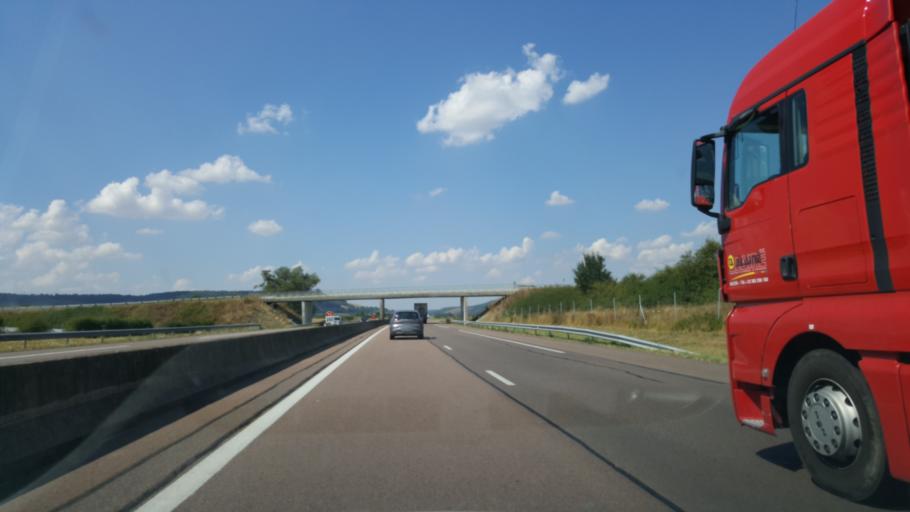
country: FR
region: Bourgogne
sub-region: Departement de la Cote-d'Or
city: Pouilly-en-Auxois
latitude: 47.2730
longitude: 4.5122
